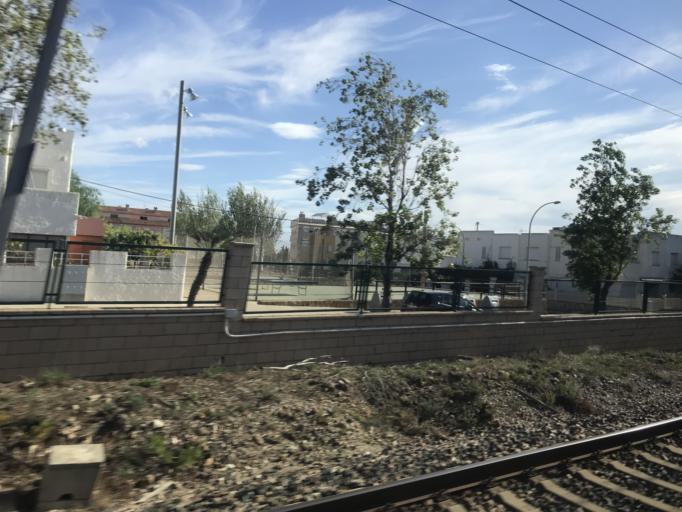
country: ES
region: Catalonia
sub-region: Provincia de Tarragona
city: L'Ampolla
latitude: 40.8162
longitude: 0.7154
